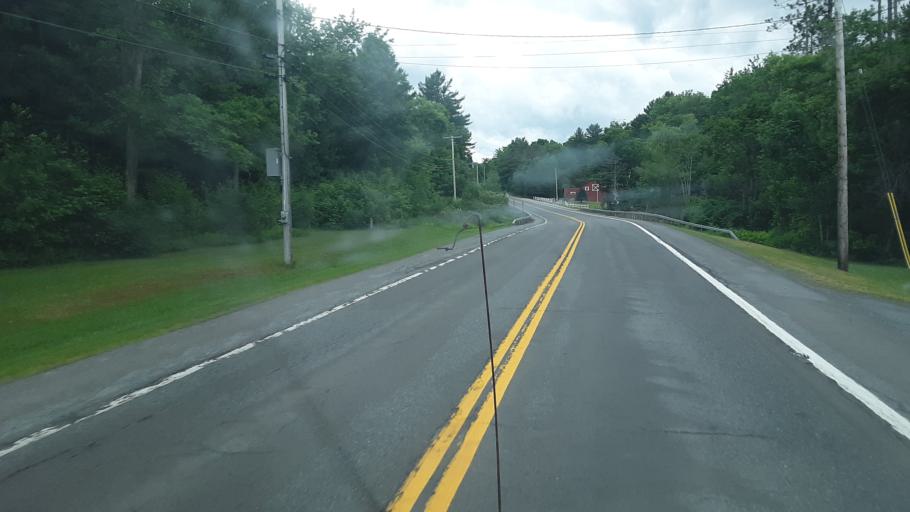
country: US
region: New York
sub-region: Oneida County
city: Rome
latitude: 43.3589
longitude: -75.4784
